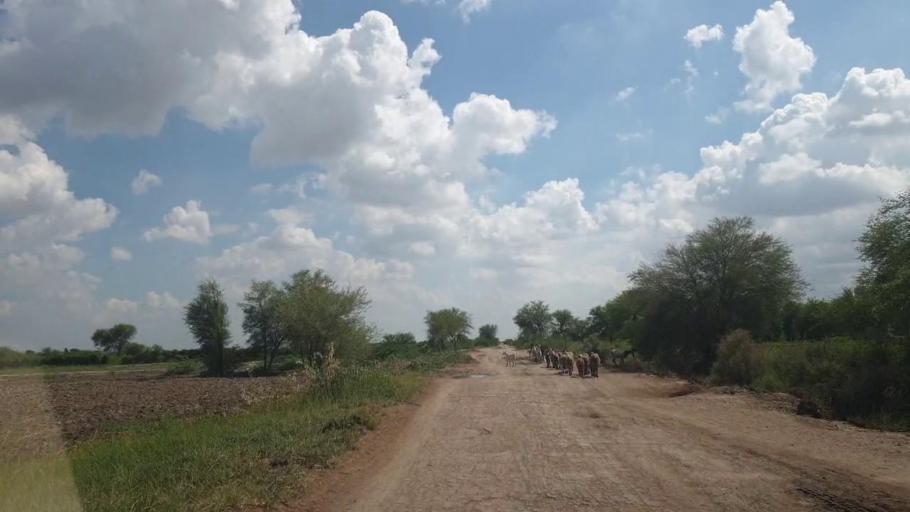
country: PK
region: Sindh
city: Pithoro
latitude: 25.6121
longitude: 69.4115
